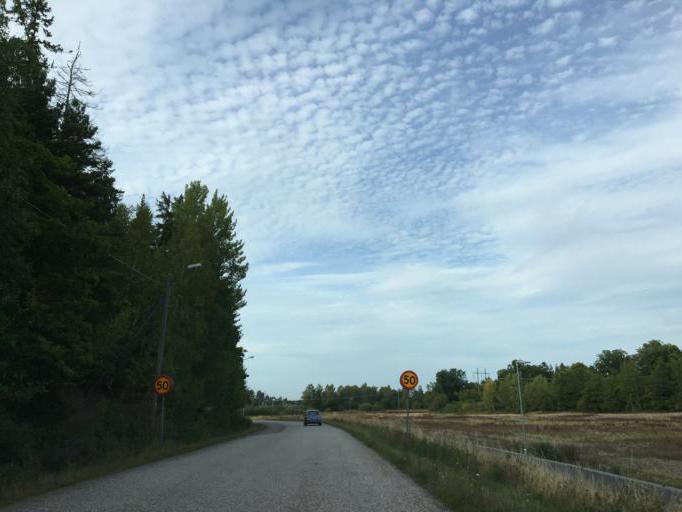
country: SE
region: Soedermanland
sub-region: Eskilstuna Kommun
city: Torshalla
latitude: 59.4480
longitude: 16.4690
